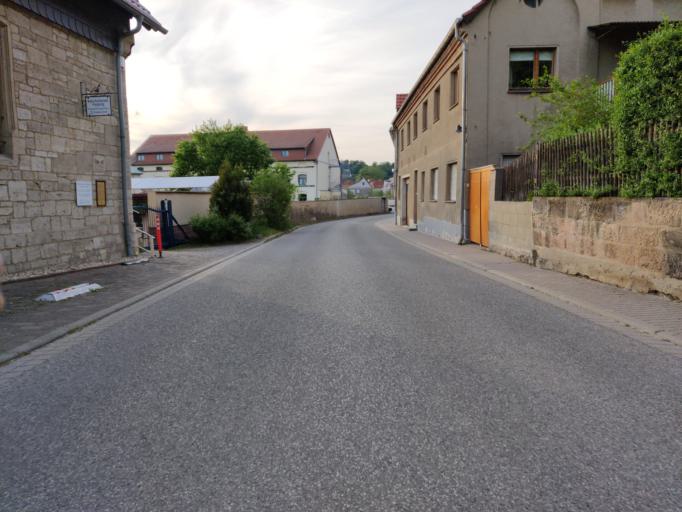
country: DE
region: Saxony-Anhalt
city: Freyburg
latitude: 51.2079
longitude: 11.7725
